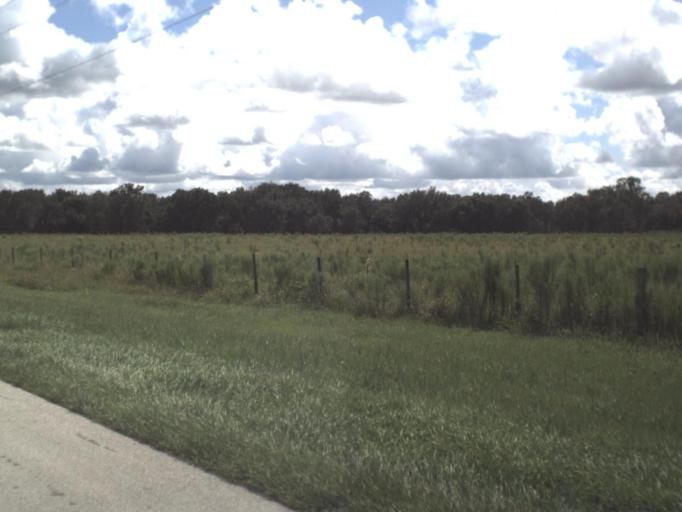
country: US
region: Florida
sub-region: DeSoto County
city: Arcadia
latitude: 27.2584
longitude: -81.9754
